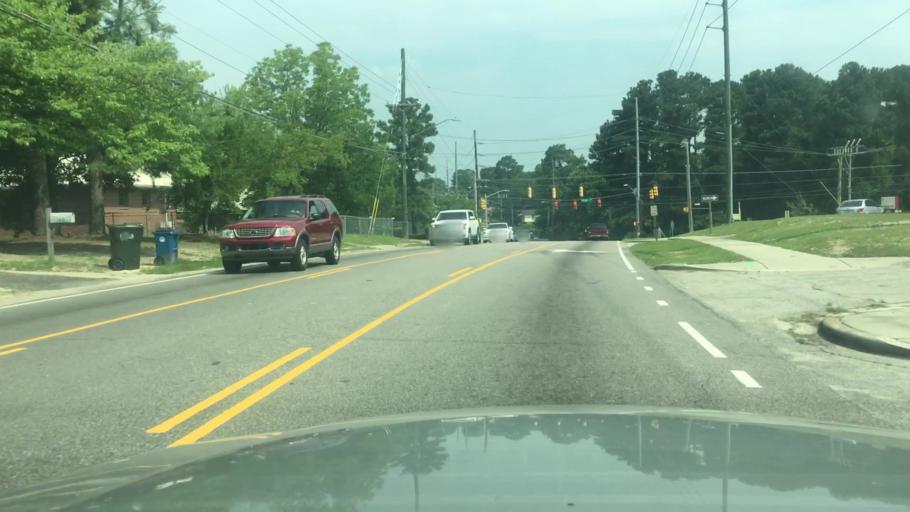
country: US
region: North Carolina
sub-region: Cumberland County
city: Hope Mills
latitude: 35.0248
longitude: -78.9420
